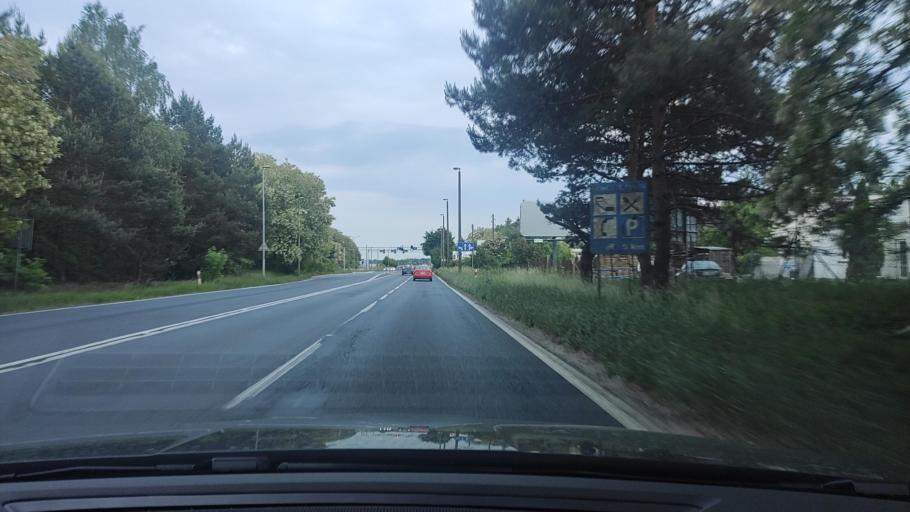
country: PL
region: Greater Poland Voivodeship
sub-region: Powiat poznanski
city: Czerwonak
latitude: 52.4177
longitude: 17.0208
